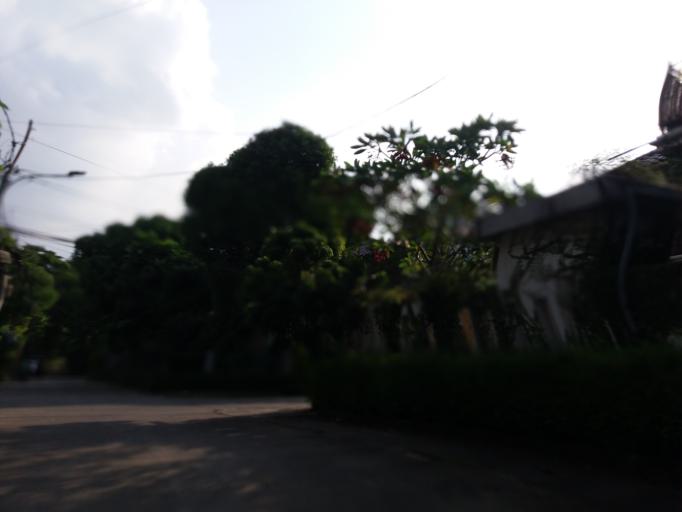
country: ID
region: Jakarta Raya
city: Jakarta
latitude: -6.2478
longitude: 106.8102
